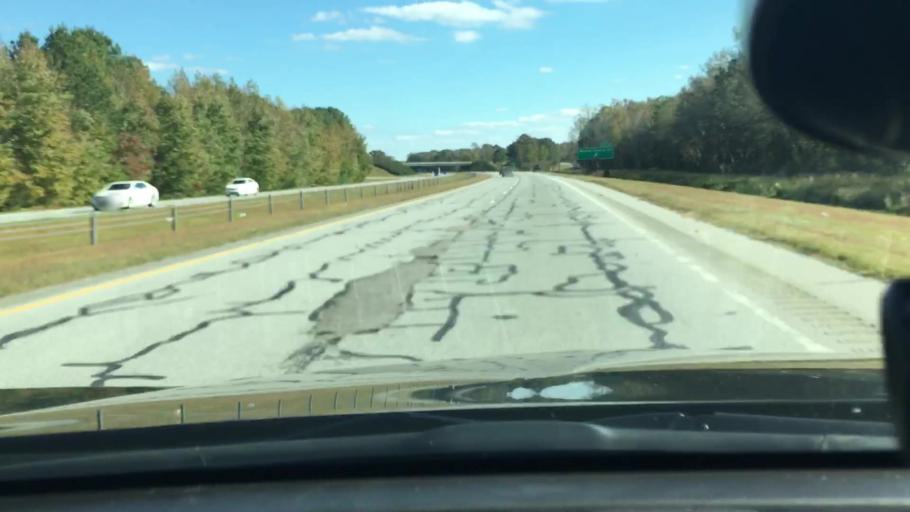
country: US
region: North Carolina
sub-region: Pitt County
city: Farmville
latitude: 35.6020
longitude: -77.5635
